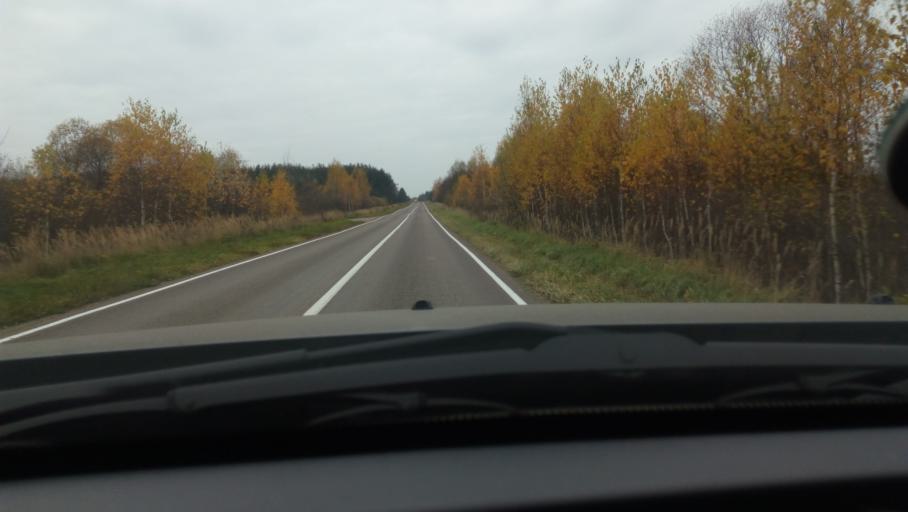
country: RU
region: Moskovskaya
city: Avsyunino
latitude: 55.5965
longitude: 39.2431
